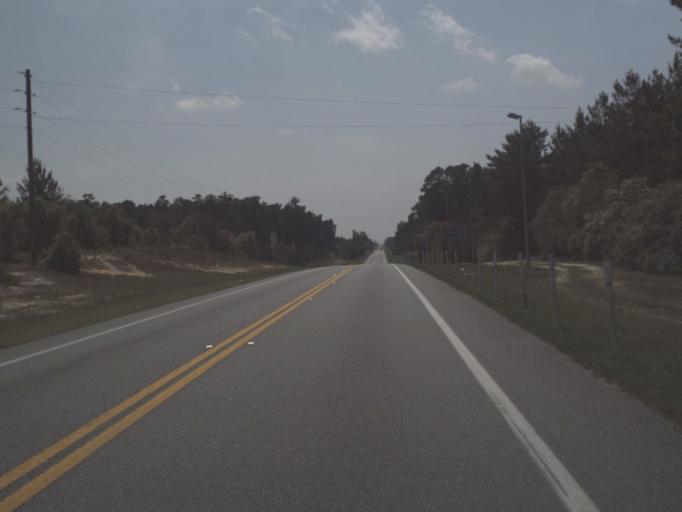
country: US
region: Florida
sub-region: Lake County
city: Astor
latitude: 29.1677
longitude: -81.6423
